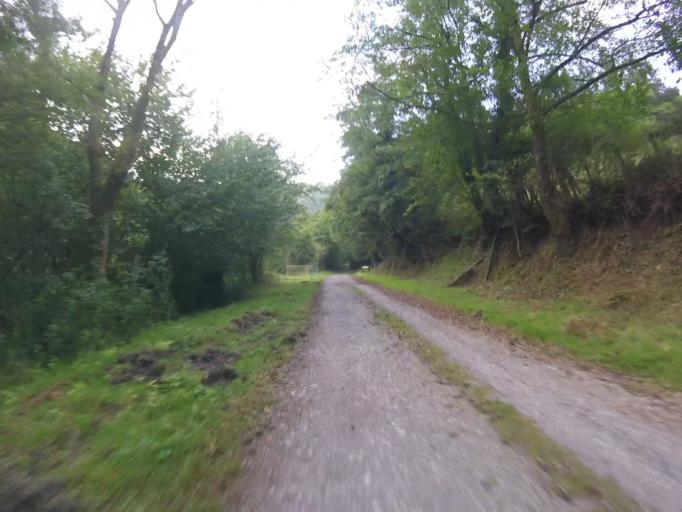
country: ES
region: Basque Country
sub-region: Provincia de Guipuzcoa
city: Berastegui
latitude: 43.1686
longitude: -1.9601
